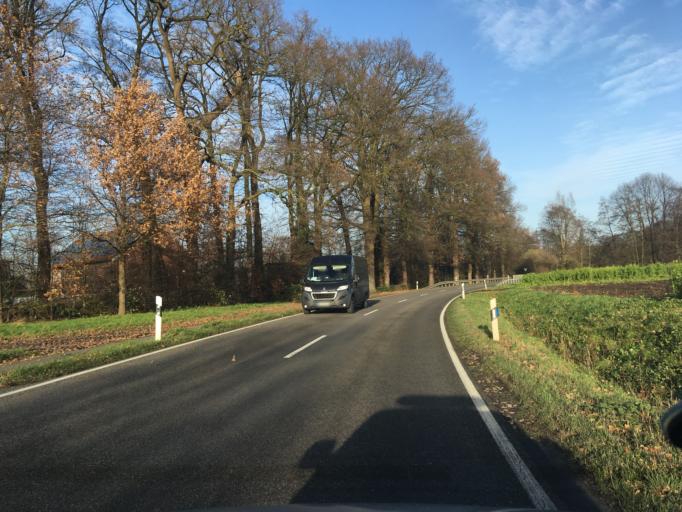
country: DE
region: North Rhine-Westphalia
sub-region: Regierungsbezirk Munster
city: Gescher
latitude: 51.9428
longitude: 7.0473
